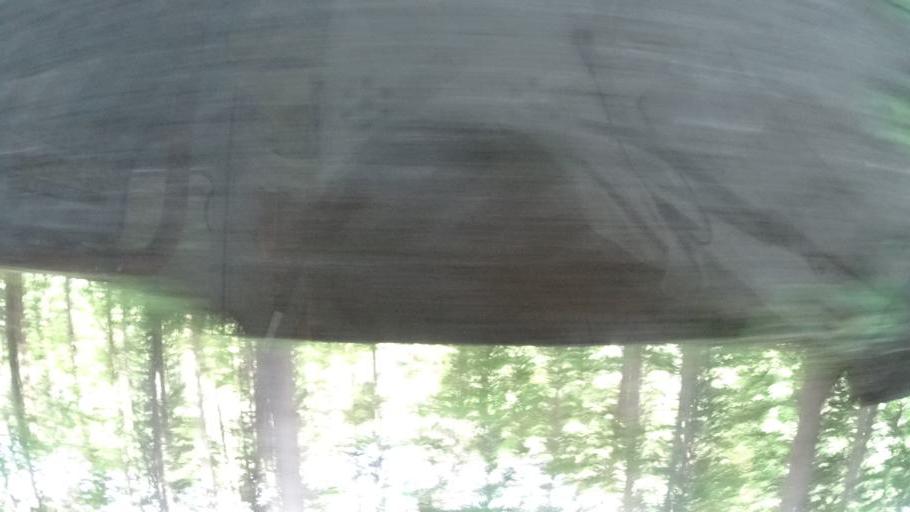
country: JP
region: Tochigi
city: Nikko
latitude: 36.6894
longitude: 139.4987
